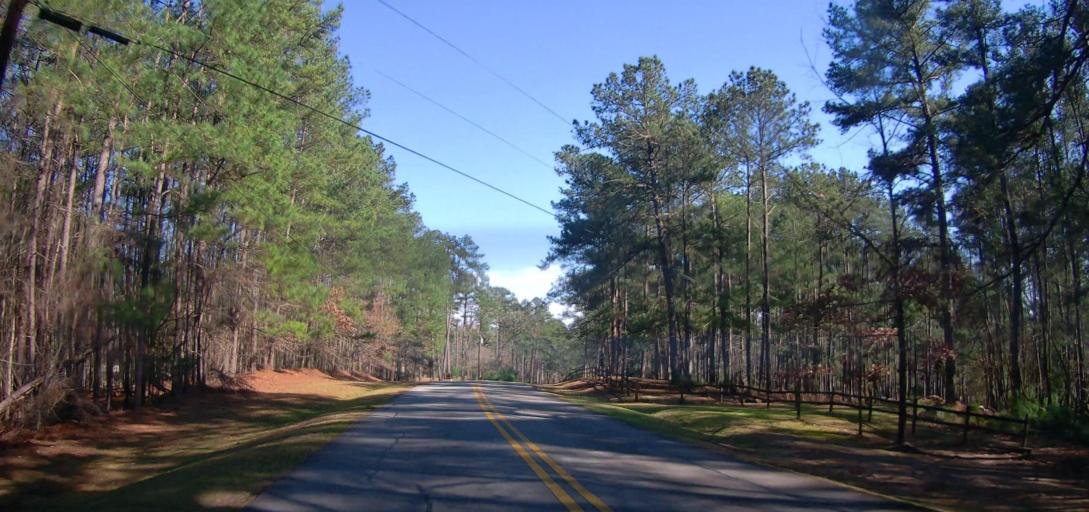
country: US
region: Georgia
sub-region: Butts County
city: Indian Springs
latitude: 33.2518
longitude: -83.9275
